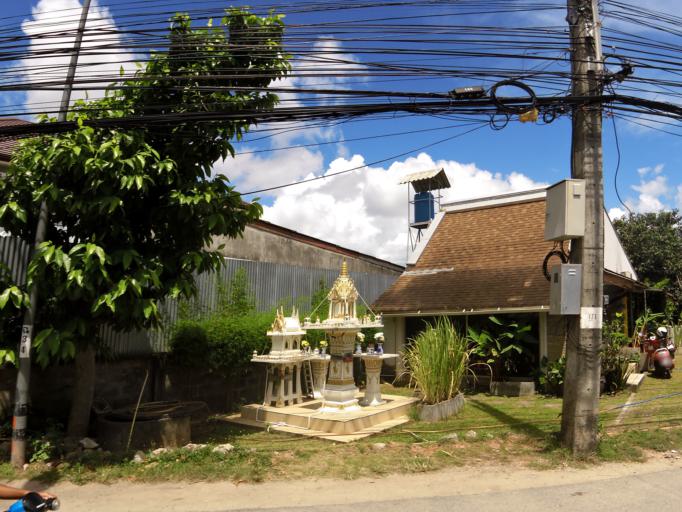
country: TH
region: Phuket
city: Ban Chalong
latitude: 7.8309
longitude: 98.3401
